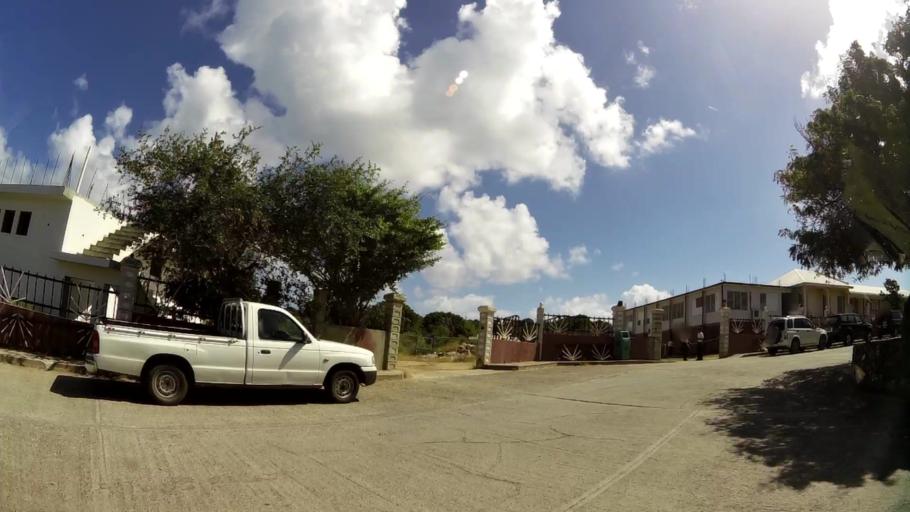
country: VG
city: Tortola
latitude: 18.4379
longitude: -64.4382
